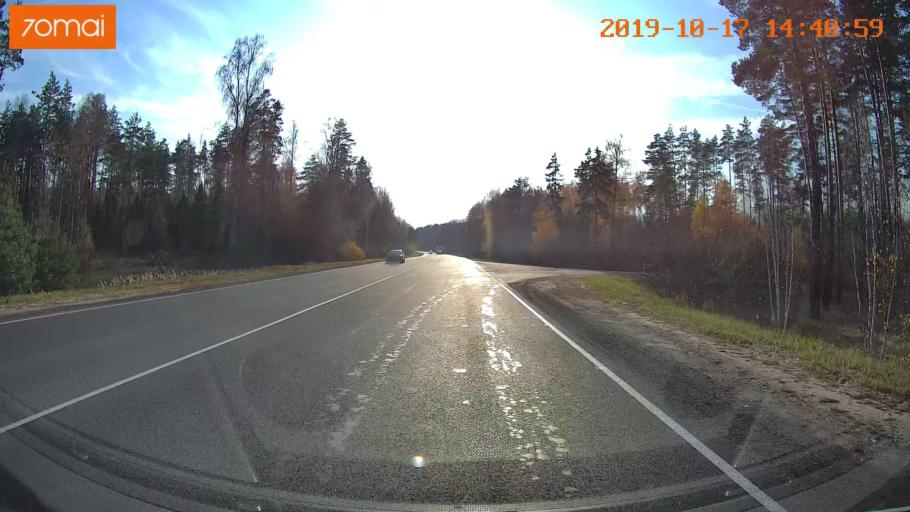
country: RU
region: Rjazan
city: Solotcha
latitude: 54.8507
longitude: 39.9456
